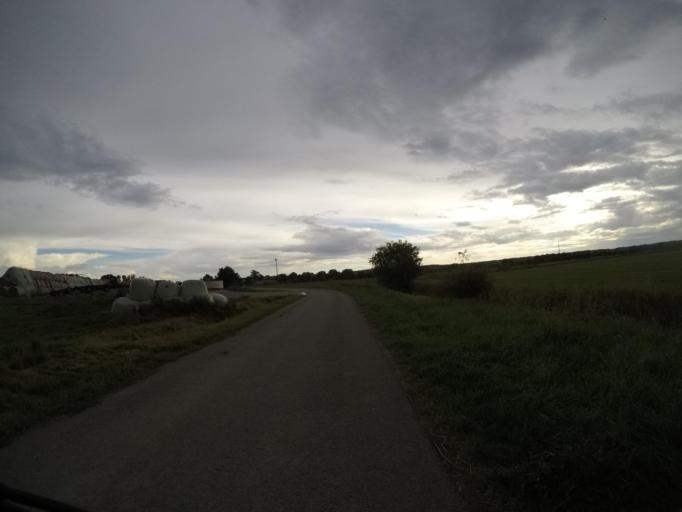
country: DE
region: Lower Saxony
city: Neu Darchau
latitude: 53.2537
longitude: 10.8739
